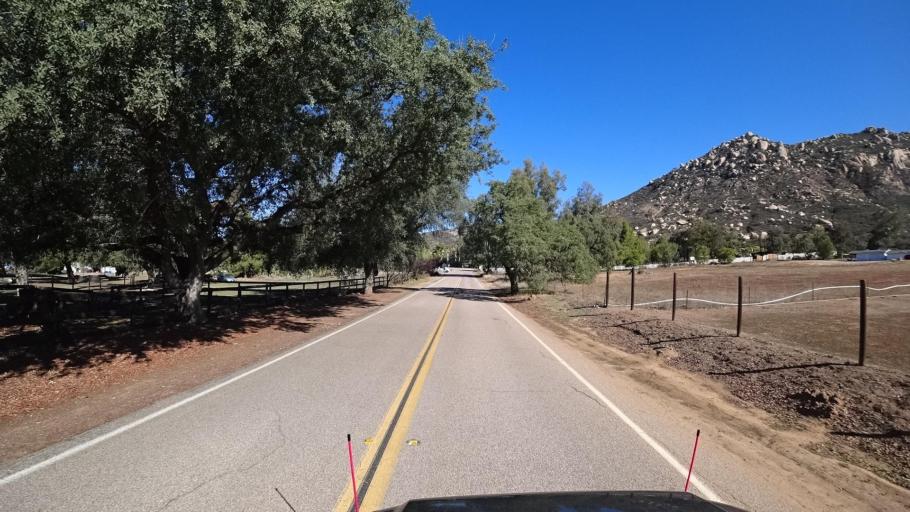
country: US
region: California
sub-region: San Diego County
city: Jamul
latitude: 32.7175
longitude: -116.8034
